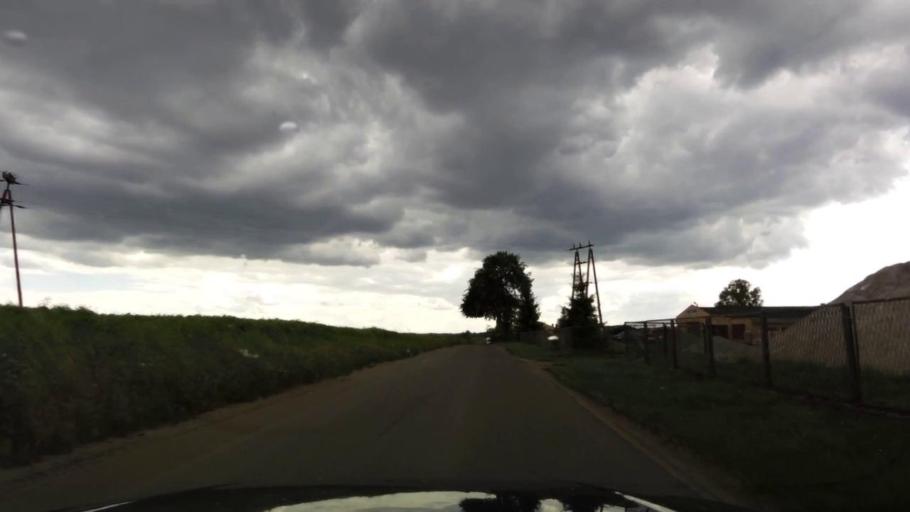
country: PL
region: West Pomeranian Voivodeship
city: Trzcinsko Zdroj
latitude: 52.9559
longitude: 14.6088
